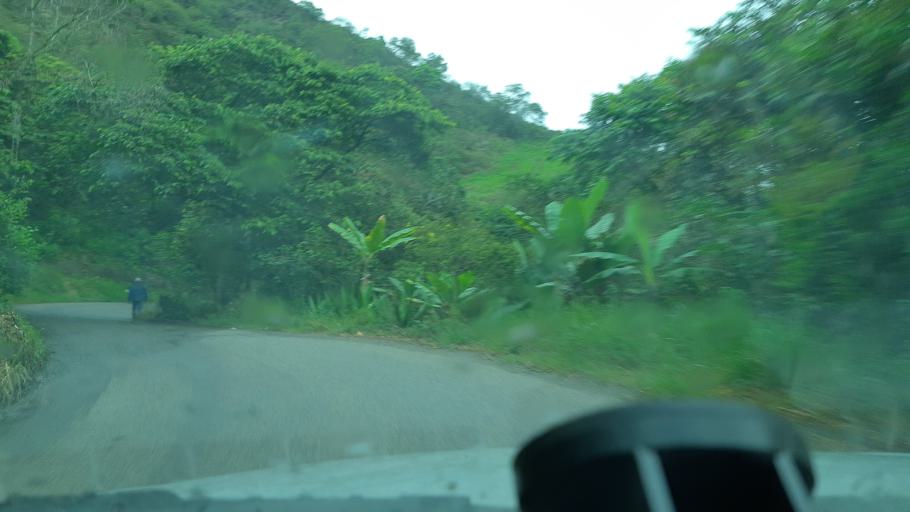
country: CO
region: Boyaca
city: Chinavita
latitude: 5.1892
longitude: -73.3816
